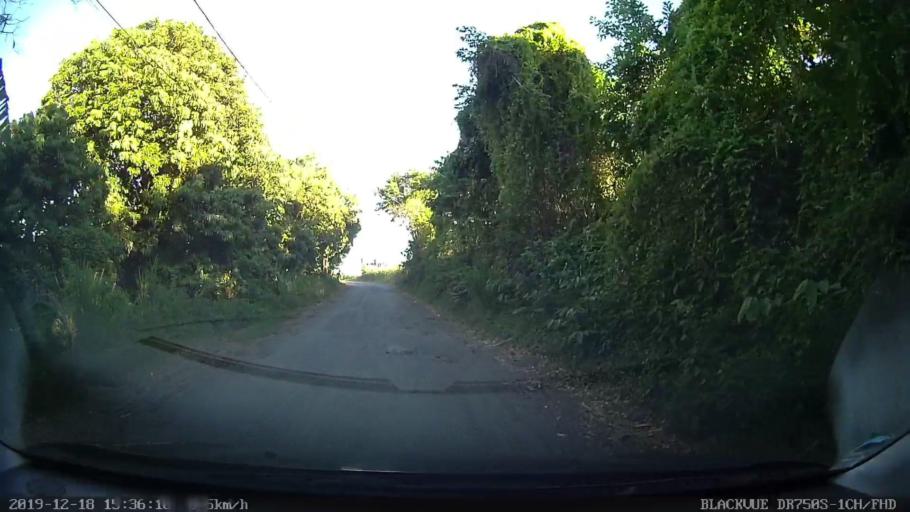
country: RE
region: Reunion
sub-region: Reunion
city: Bras-Panon
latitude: -20.9954
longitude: 55.6634
